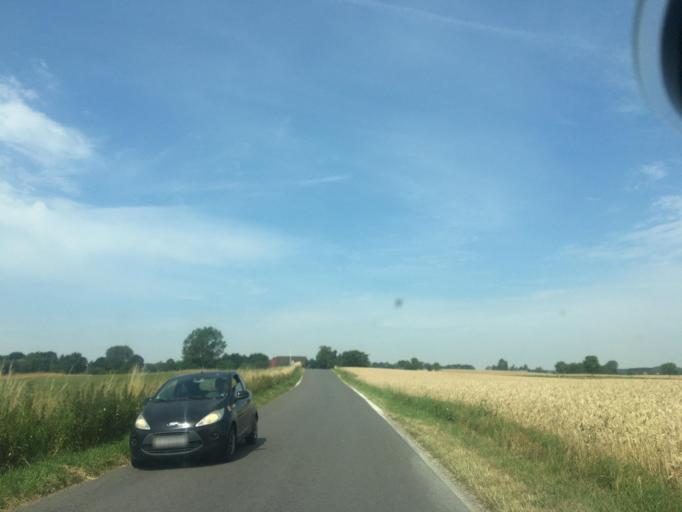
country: DK
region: Zealand
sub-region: Faxe Kommune
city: Ronnede
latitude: 55.1974
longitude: 12.0540
